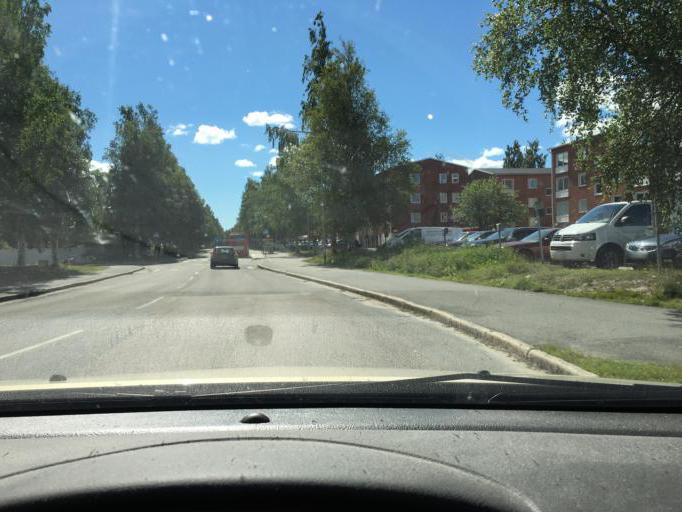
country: SE
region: Norrbotten
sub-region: Lulea Kommun
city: Lulea
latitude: 65.6008
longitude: 22.1325
